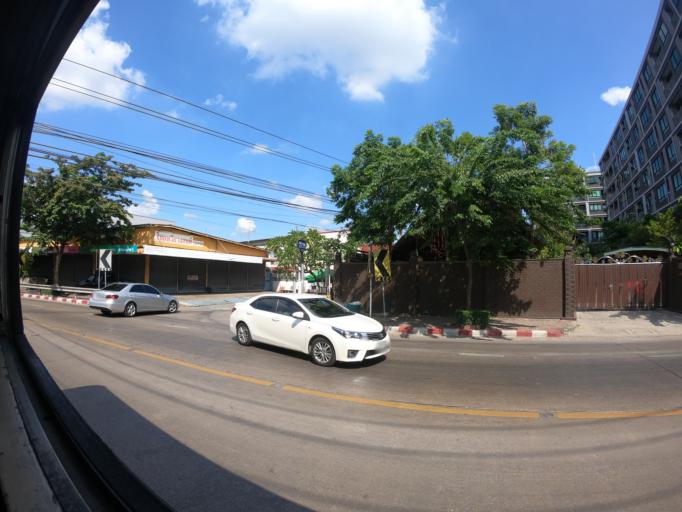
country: TH
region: Bangkok
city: Lat Phrao
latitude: 13.8166
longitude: 100.6104
